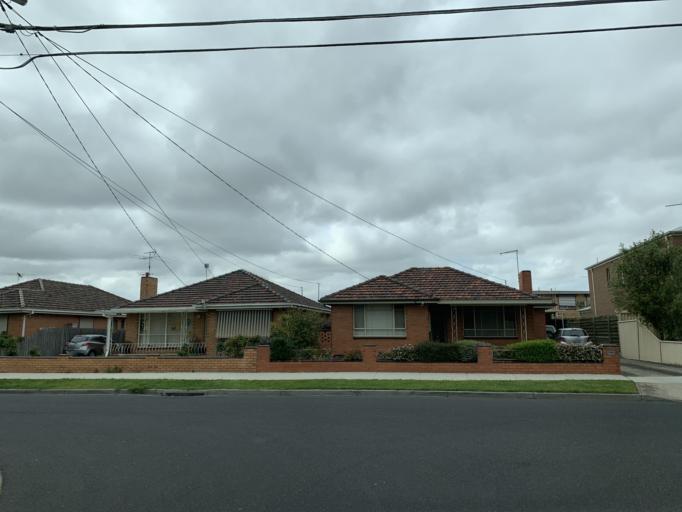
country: AU
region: Victoria
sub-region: Moonee Valley
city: Essendon West
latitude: -37.7586
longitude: 144.8593
